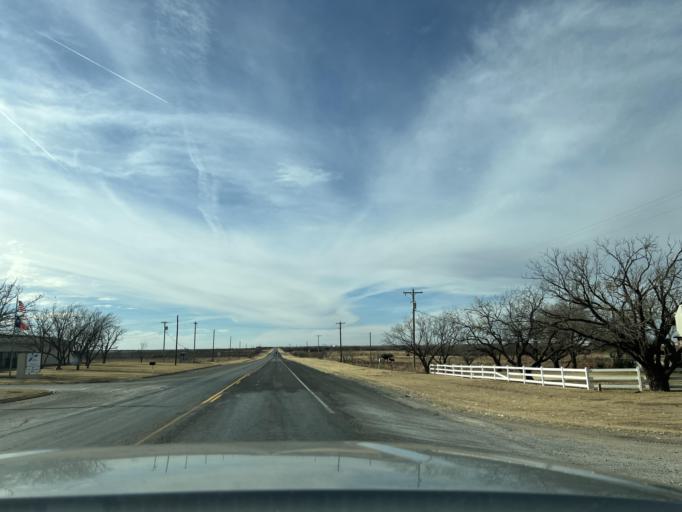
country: US
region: Texas
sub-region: Jones County
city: Anson
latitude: 32.7519
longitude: -99.9225
